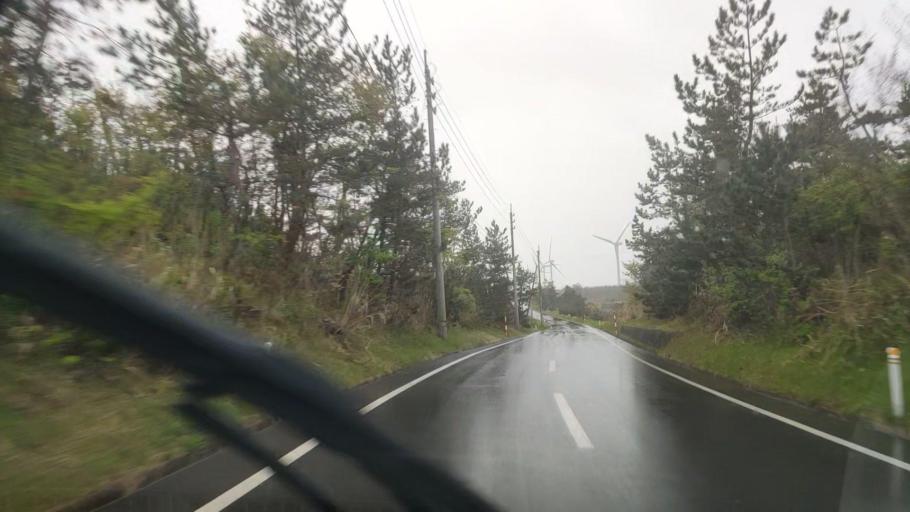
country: JP
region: Akita
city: Noshiromachi
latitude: 40.0790
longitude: 139.9538
